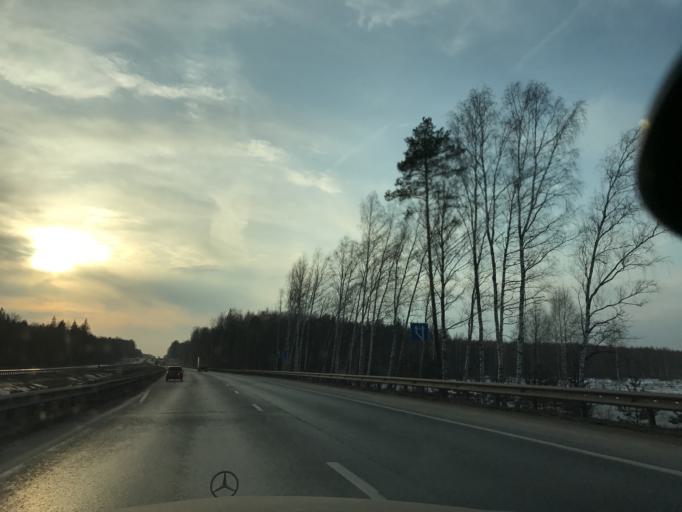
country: RU
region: Vladimir
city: Kosterevo
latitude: 55.9549
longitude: 39.5993
